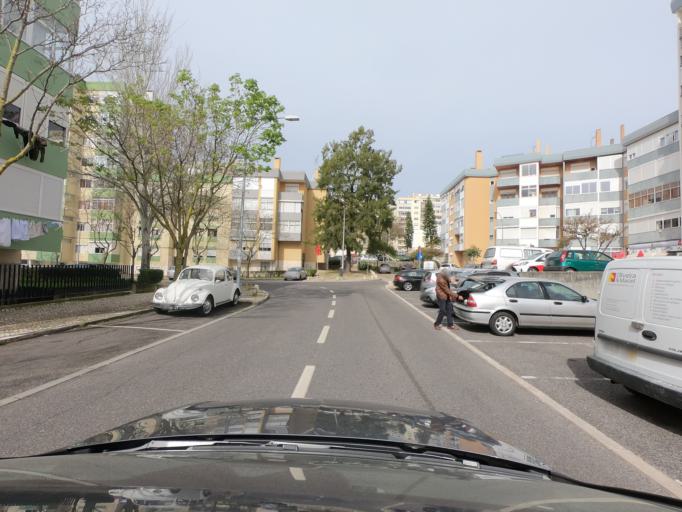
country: PT
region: Lisbon
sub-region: Oeiras
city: Oeiras
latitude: 38.6952
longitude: -9.3028
